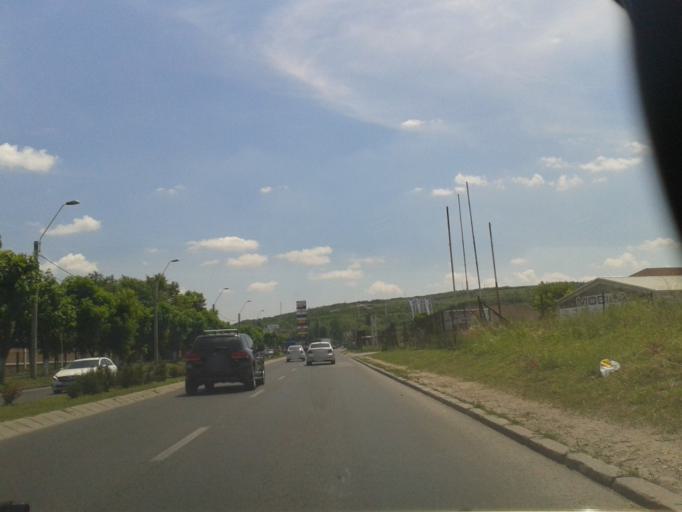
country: RO
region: Hunedoara
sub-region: Municipiul Deva
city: Deva
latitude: 45.8657
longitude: 22.9233
